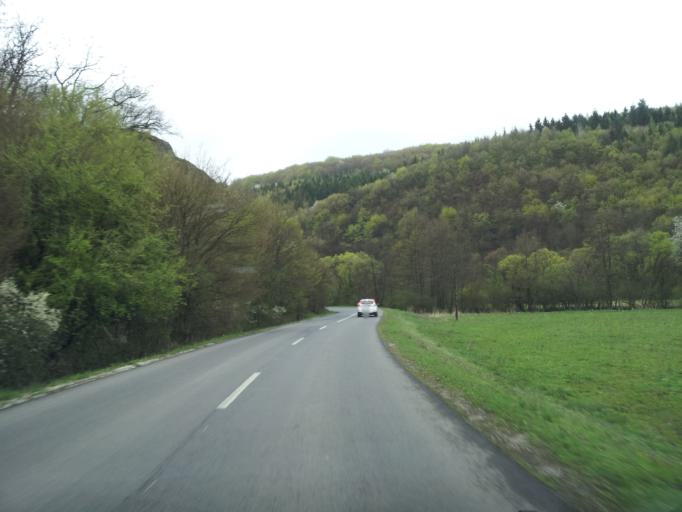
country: HU
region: Borsod-Abauj-Zemplen
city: Rudabanya
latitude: 48.4798
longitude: 20.5721
